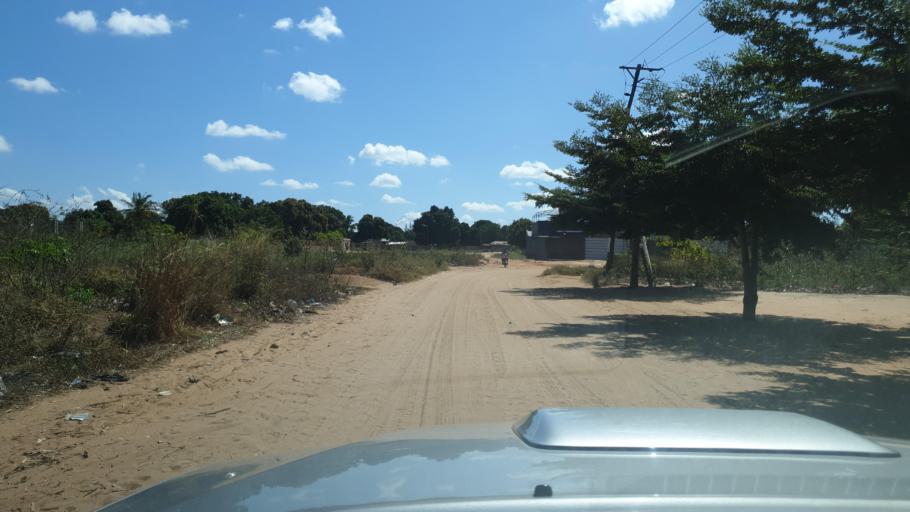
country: MZ
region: Nampula
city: Nampula
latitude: -15.1026
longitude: 39.2059
